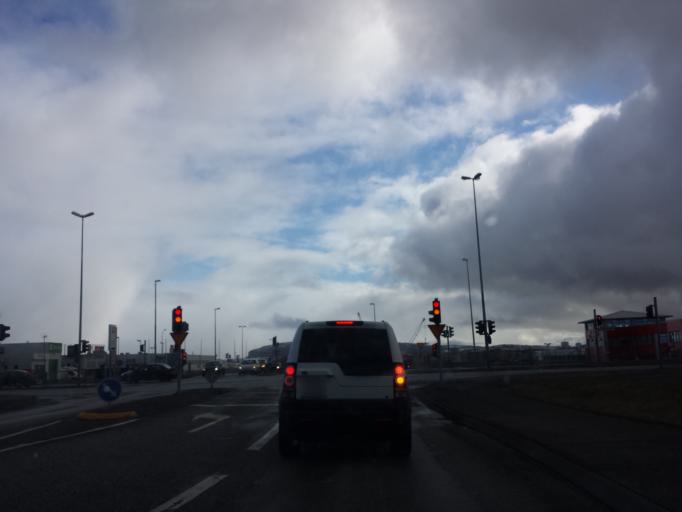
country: IS
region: Capital Region
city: Reykjavik
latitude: 64.1406
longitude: -21.8512
